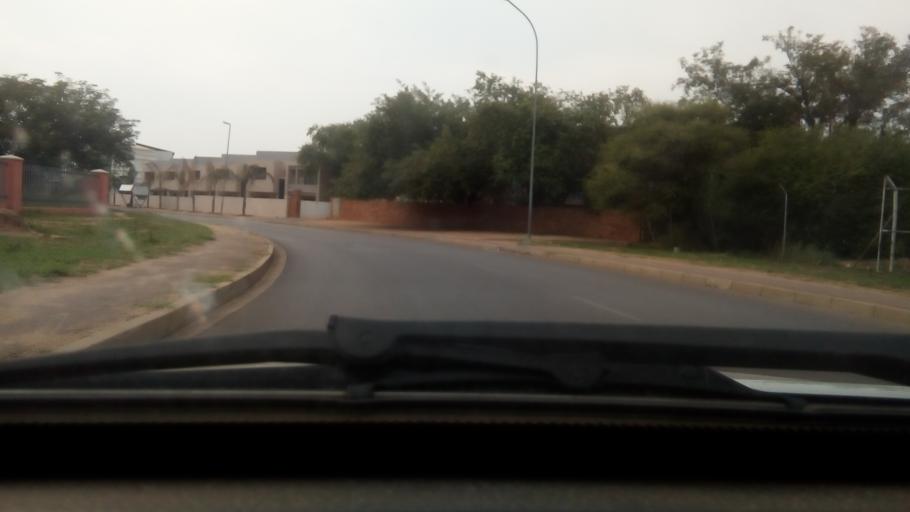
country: BW
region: South East
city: Gaborone
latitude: -24.6663
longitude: 25.9347
